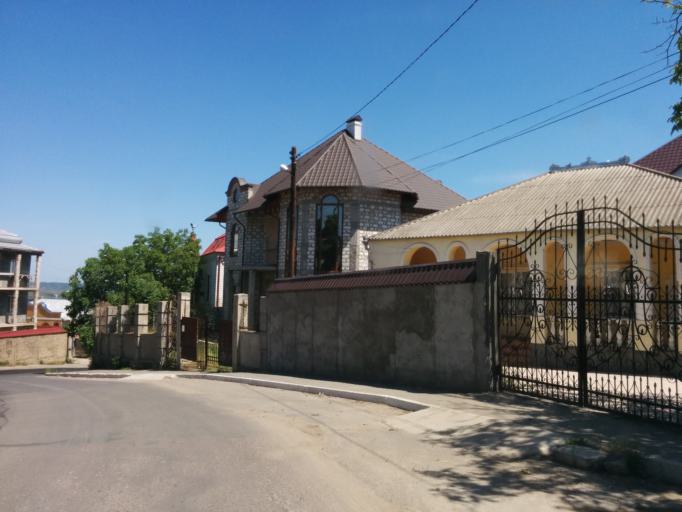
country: MD
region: Raionul Soroca
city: Soroca
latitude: 48.1605
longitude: 28.2946
